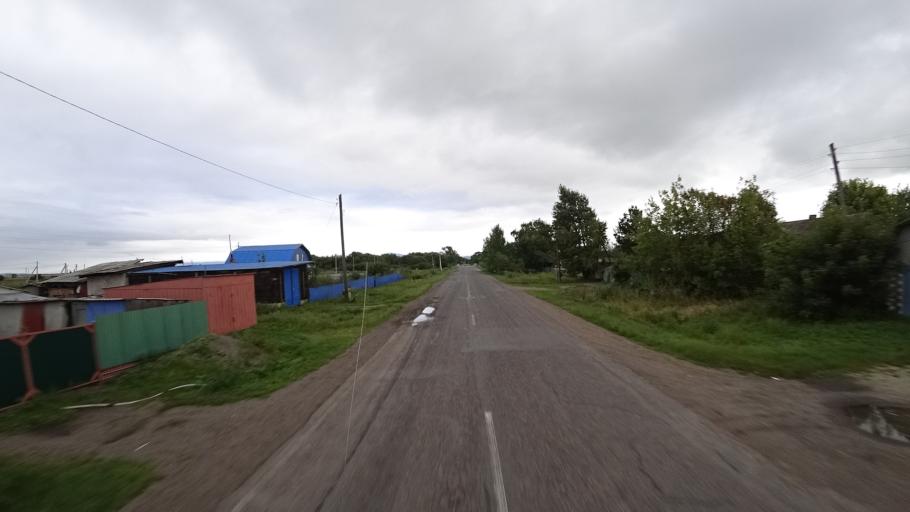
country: RU
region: Primorskiy
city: Chernigovka
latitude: 44.3541
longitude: 132.5653
